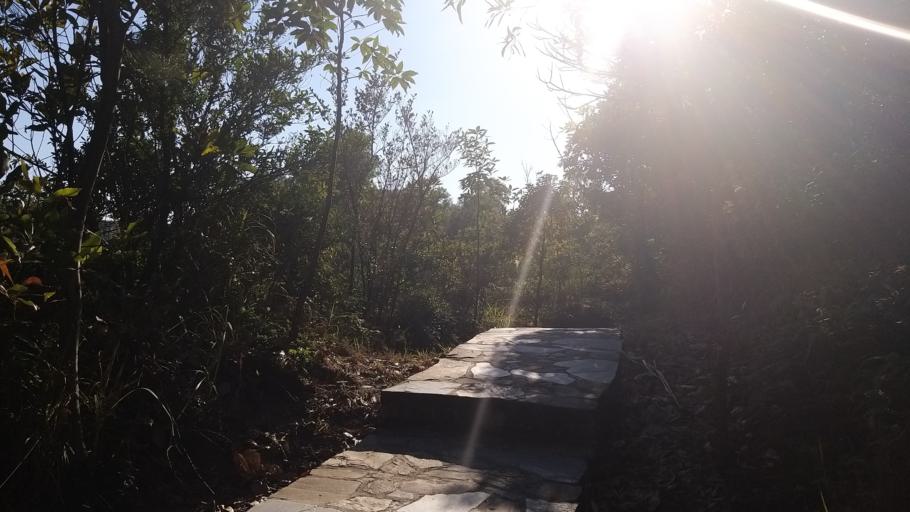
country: HK
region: Tuen Mun
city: Tuen Mun
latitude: 22.4015
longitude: 113.9881
